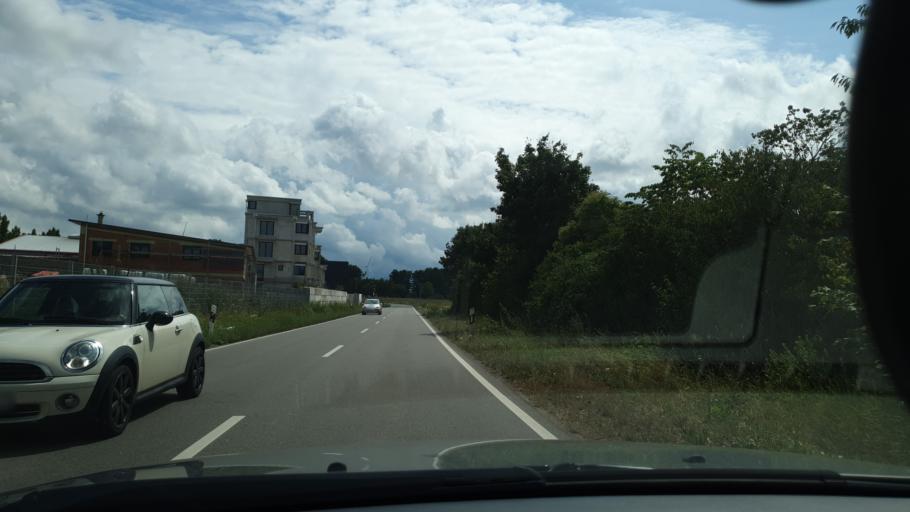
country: DE
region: Rheinland-Pfalz
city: Offenbach an der Queich
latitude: 49.1947
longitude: 8.2056
